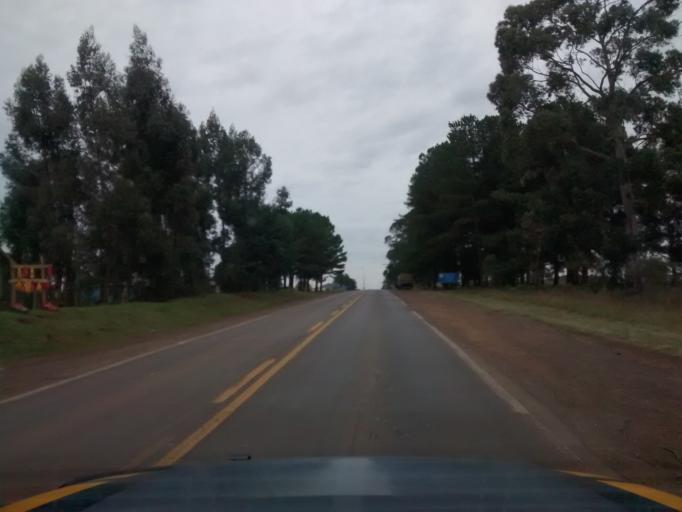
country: BR
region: Rio Grande do Sul
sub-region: Vacaria
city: Vacaria
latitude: -28.4951
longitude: -50.9138
